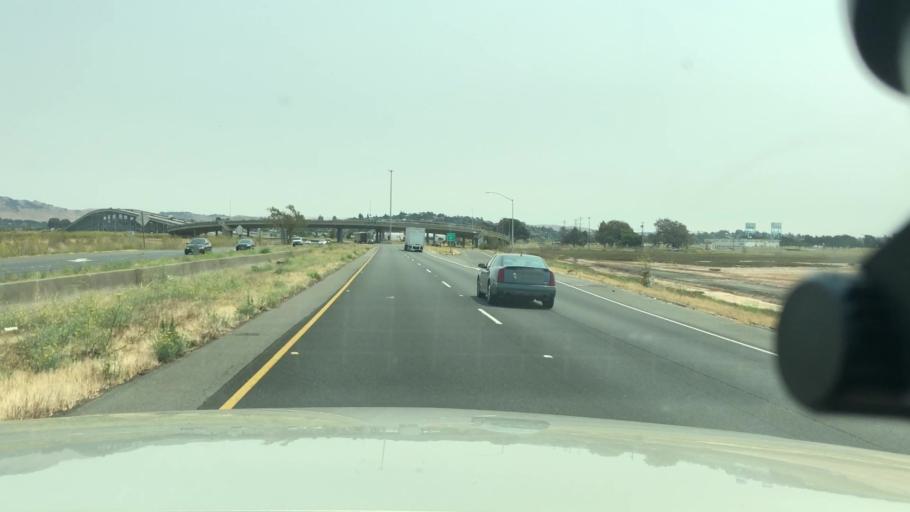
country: US
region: California
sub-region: Solano County
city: Vallejo
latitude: 38.1173
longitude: -122.2929
